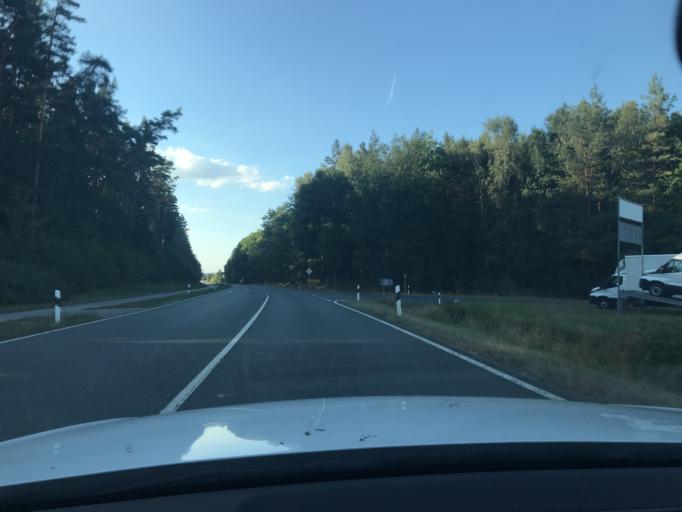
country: DE
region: Bavaria
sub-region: Upper Franconia
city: Emtmannsberg
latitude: 49.8935
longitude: 11.6130
